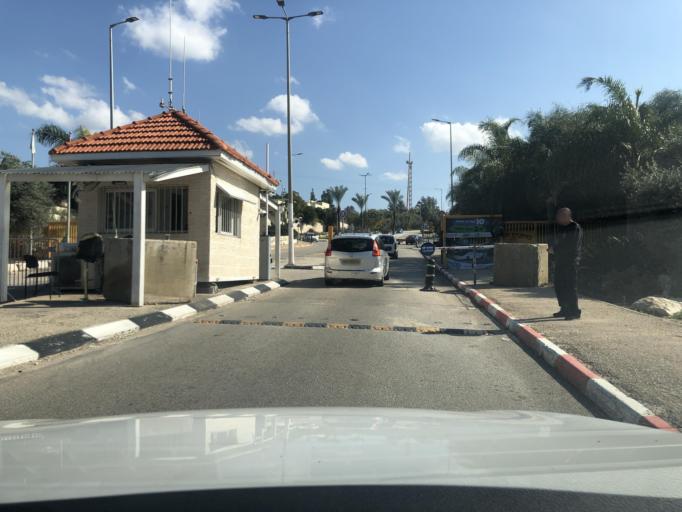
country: PS
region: West Bank
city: Azun Atme
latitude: 32.1137
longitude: 35.0333
